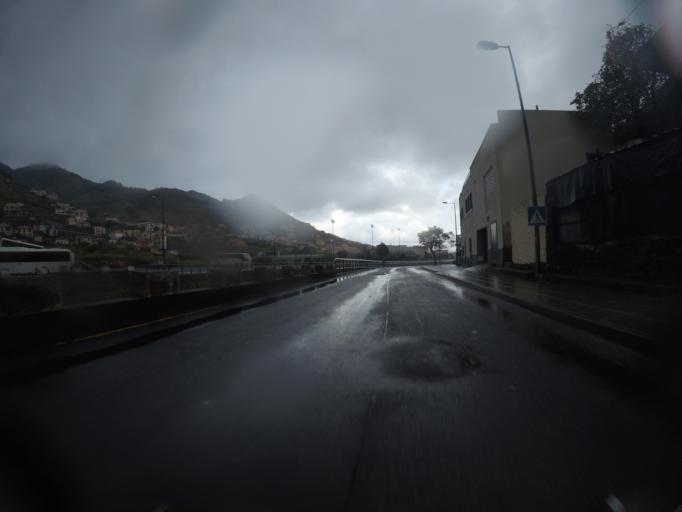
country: PT
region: Madeira
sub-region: Machico
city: Machico
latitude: 32.7279
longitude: -16.7736
